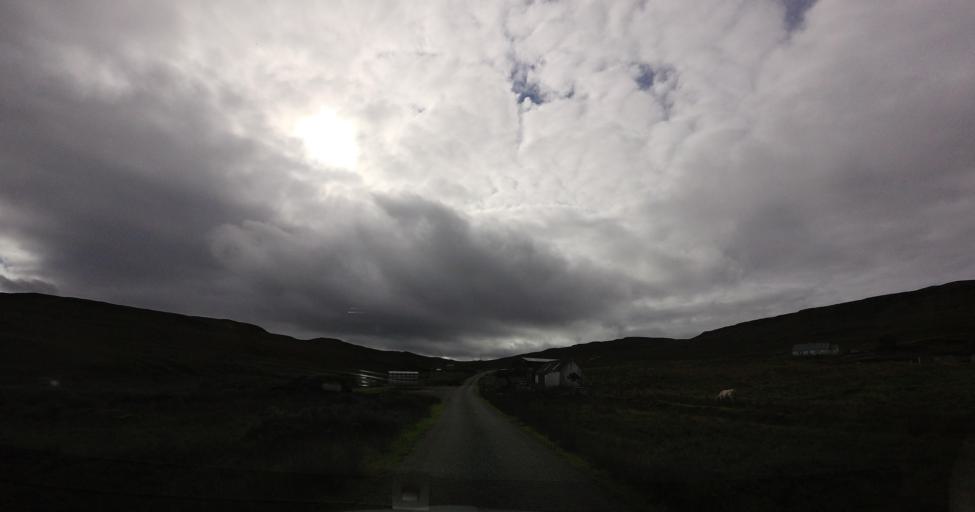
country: GB
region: Scotland
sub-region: Highland
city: Isle of Skye
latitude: 57.4194
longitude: -6.2577
